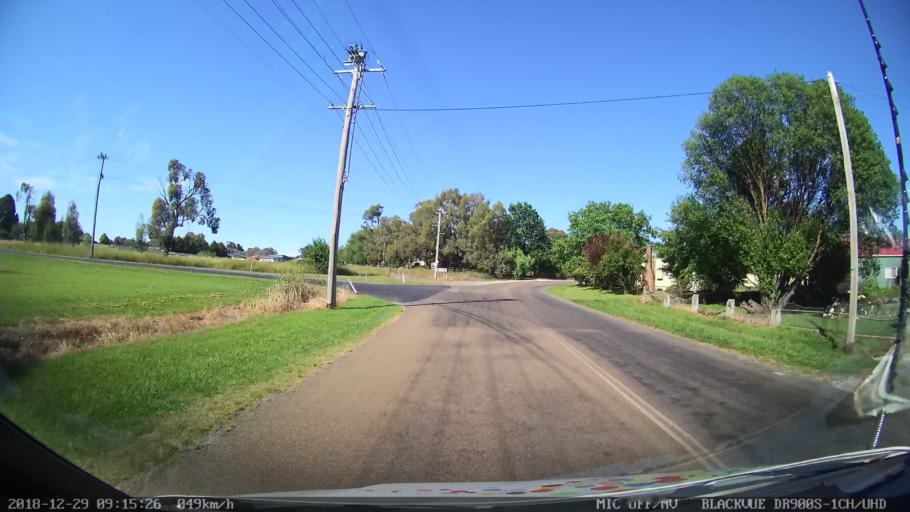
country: AU
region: New South Wales
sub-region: Upper Lachlan Shire
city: Crookwell
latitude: -34.4556
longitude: 149.4604
